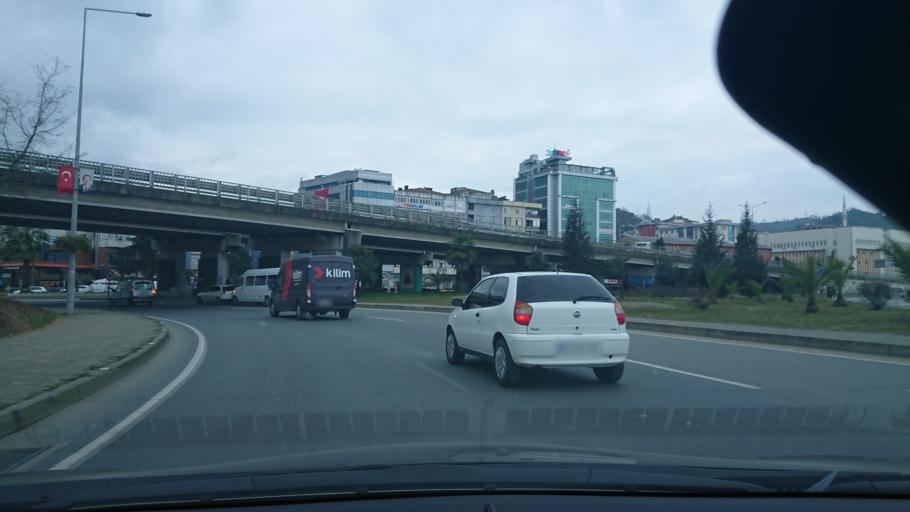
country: TR
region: Rize
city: Rize
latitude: 41.0275
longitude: 40.5192
